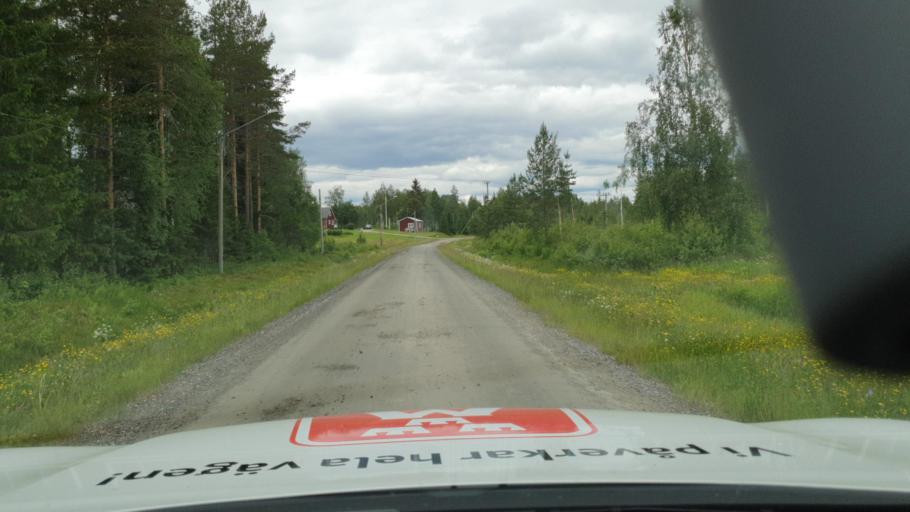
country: SE
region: Vaesterbotten
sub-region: Bjurholms Kommun
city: Bjurholm
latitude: 63.7246
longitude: 19.3117
